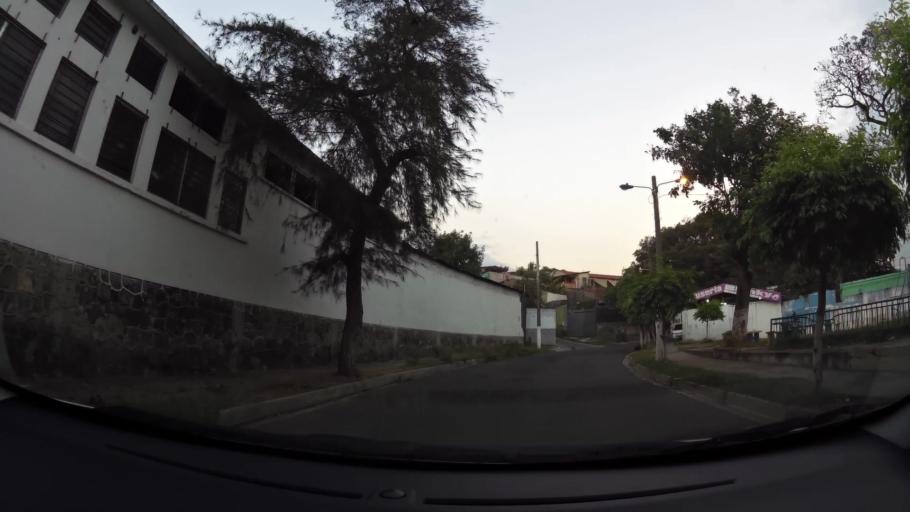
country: SV
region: San Salvador
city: San Salvador
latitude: 13.7063
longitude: -89.1856
